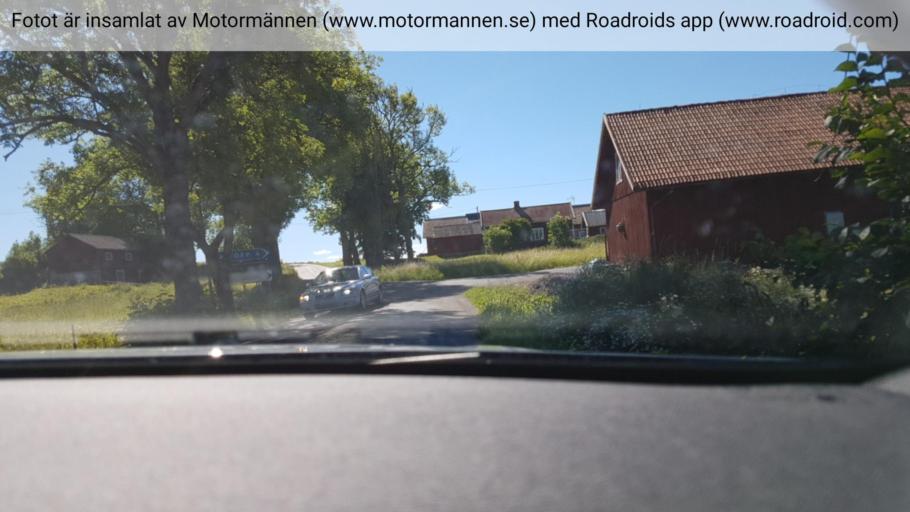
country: SE
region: Vaestra Goetaland
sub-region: Falkopings Kommun
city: Akarp
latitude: 58.2574
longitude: 13.6700
